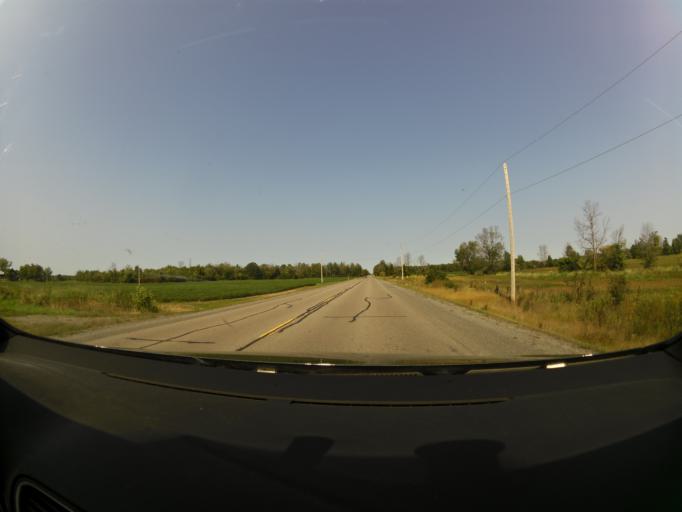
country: CA
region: Ontario
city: Arnprior
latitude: 45.4192
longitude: -76.1531
